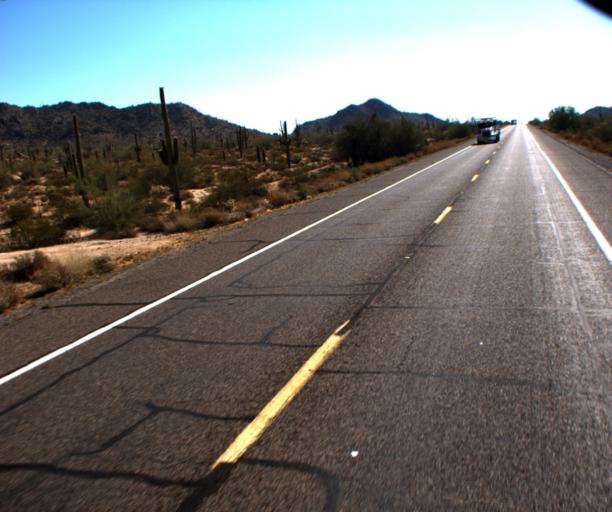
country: US
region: Arizona
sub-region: Pinal County
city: Sacaton
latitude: 33.0078
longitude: -111.7008
